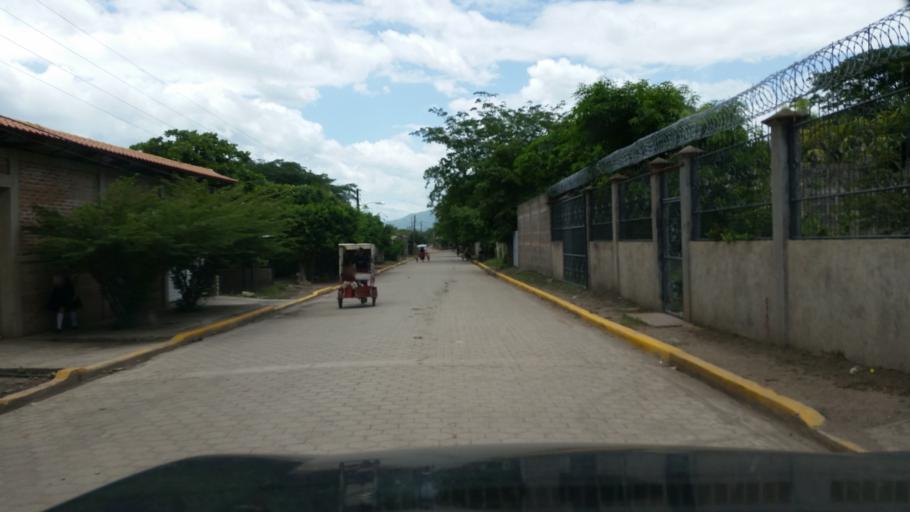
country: NI
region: Matagalpa
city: Ciudad Dario
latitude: 12.8577
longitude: -86.0918
